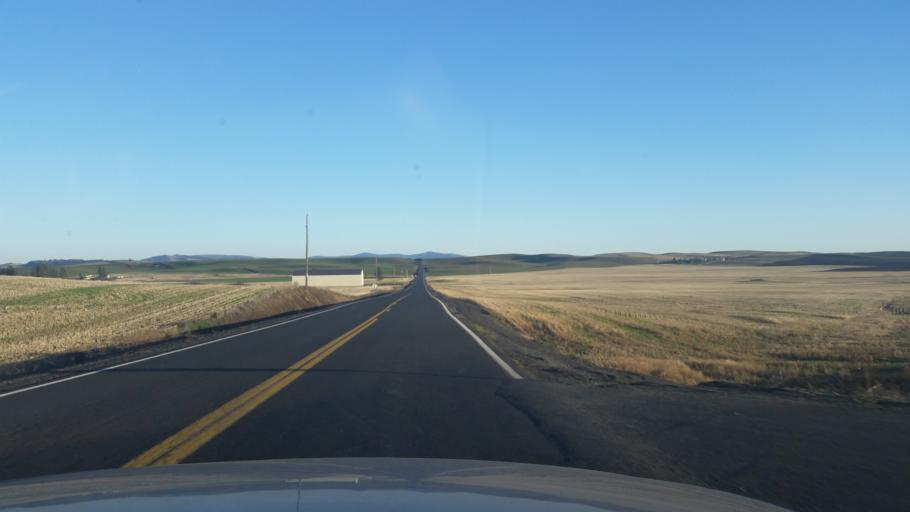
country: US
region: Washington
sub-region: Spokane County
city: Opportunity
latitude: 47.3675
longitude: -117.2922
